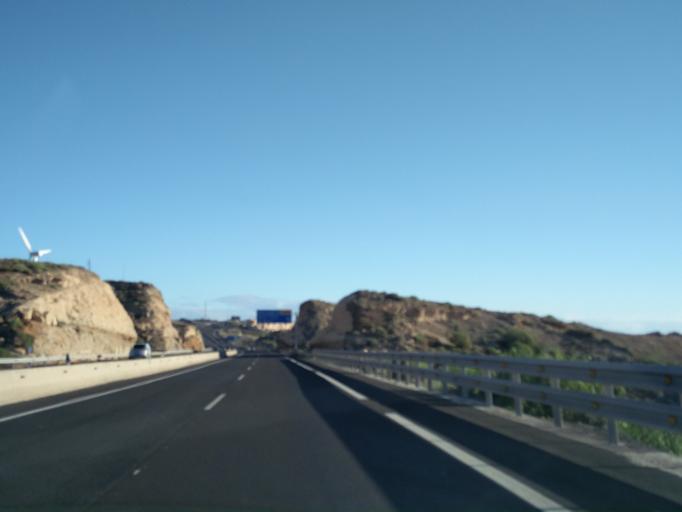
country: ES
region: Canary Islands
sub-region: Provincia de Santa Cruz de Tenerife
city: Lomo de Arico
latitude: 28.1579
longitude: -16.4393
